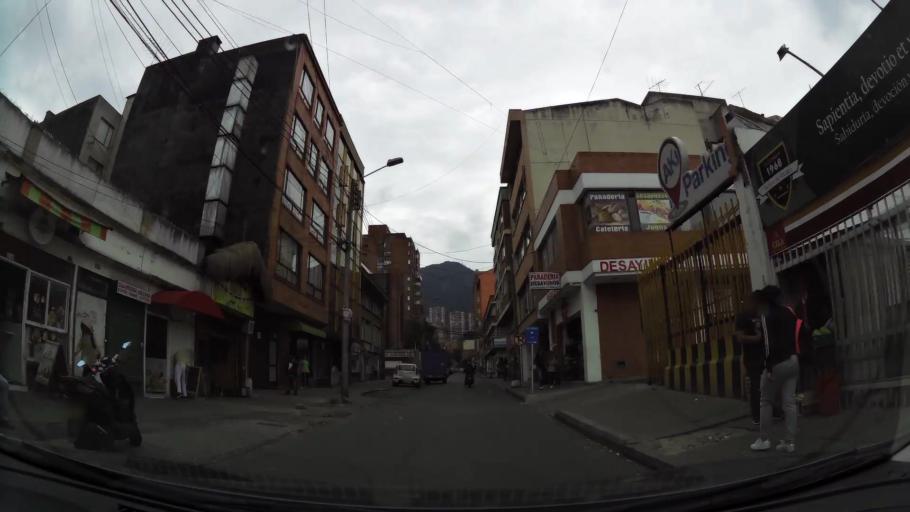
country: CO
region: Bogota D.C.
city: Bogota
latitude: 4.6475
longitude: -74.0631
